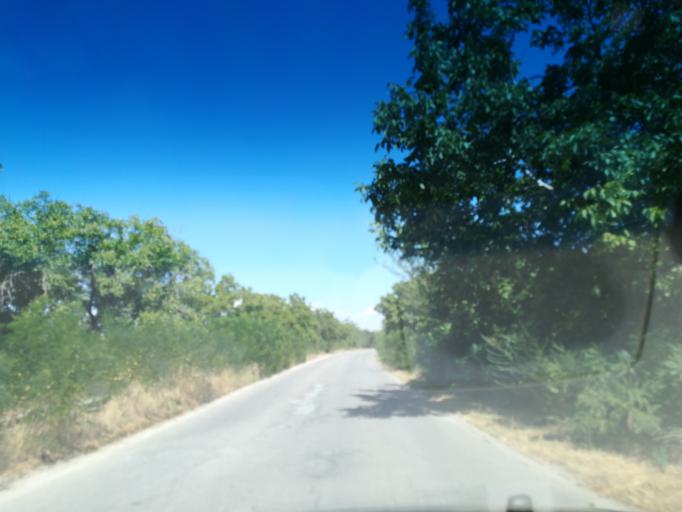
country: BG
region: Plovdiv
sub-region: Obshtina Asenovgrad
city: Asenovgrad
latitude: 42.0246
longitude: 24.9787
